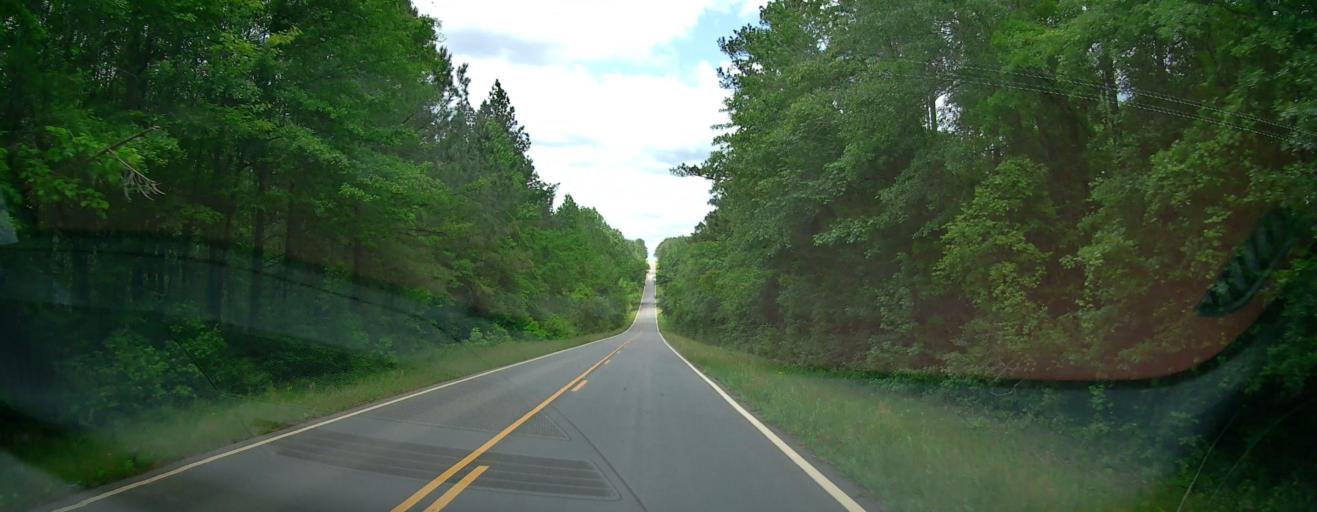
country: US
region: Georgia
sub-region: Laurens County
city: Dublin
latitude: 32.6229
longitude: -82.9750
